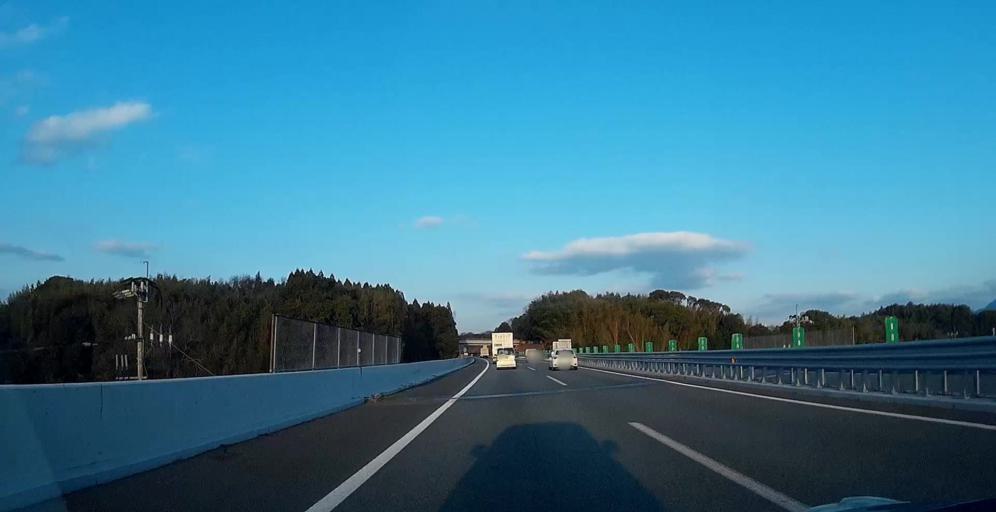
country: JP
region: Kumamoto
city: Uto
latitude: 32.6973
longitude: 130.7460
